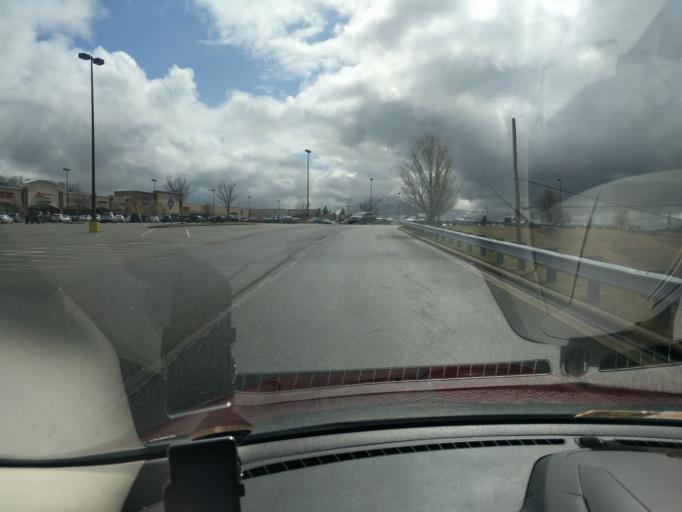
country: US
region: West Virginia
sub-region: Raleigh County
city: Stanaford
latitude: 37.8035
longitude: -81.1770
